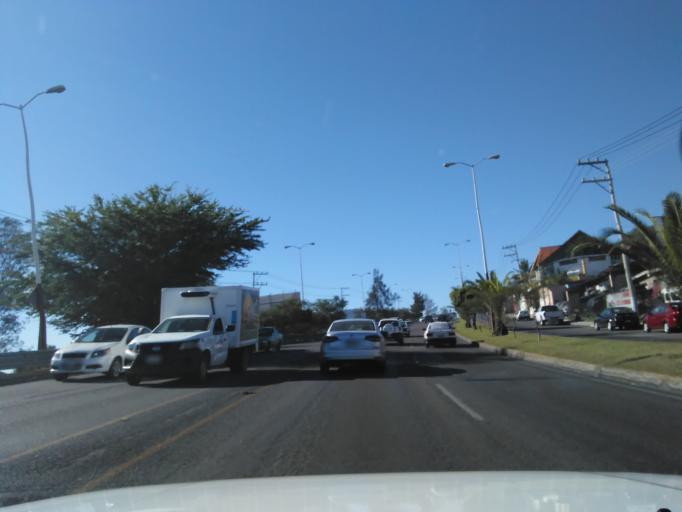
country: MX
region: Nayarit
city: Xalisco
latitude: 21.4665
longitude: -104.8884
